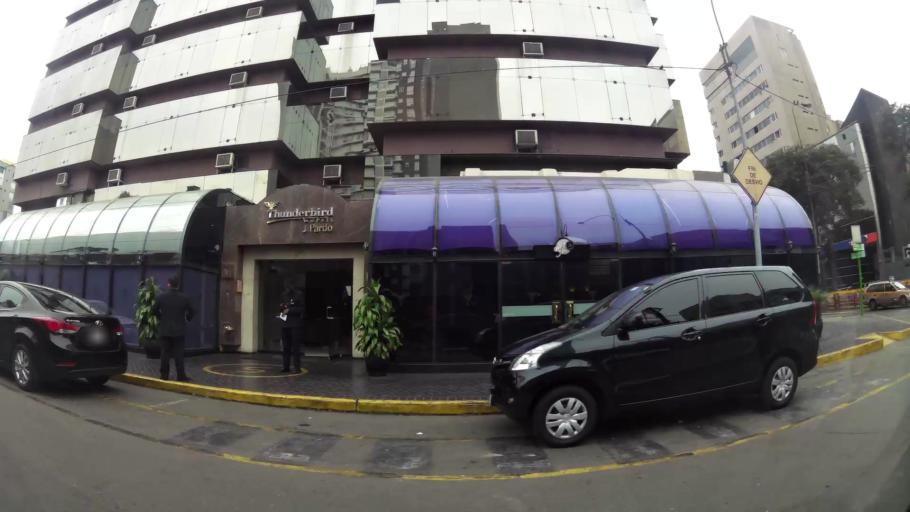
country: PE
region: Lima
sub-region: Lima
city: San Isidro
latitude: -12.1189
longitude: -77.0336
